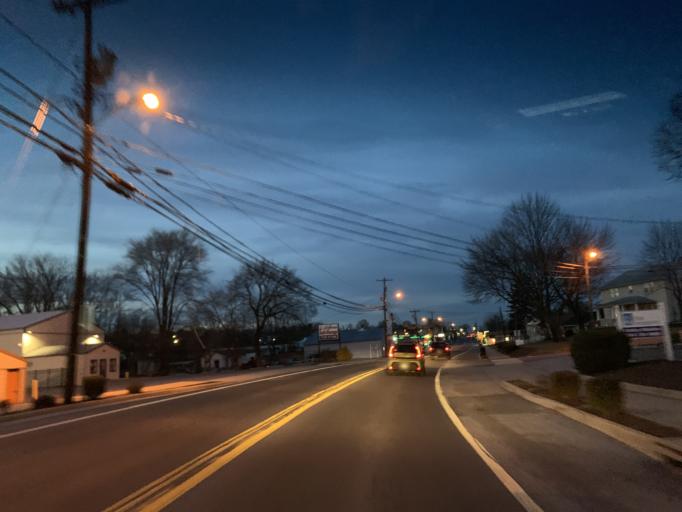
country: US
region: West Virginia
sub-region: Jefferson County
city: Ranson
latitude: 39.3013
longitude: -77.8637
